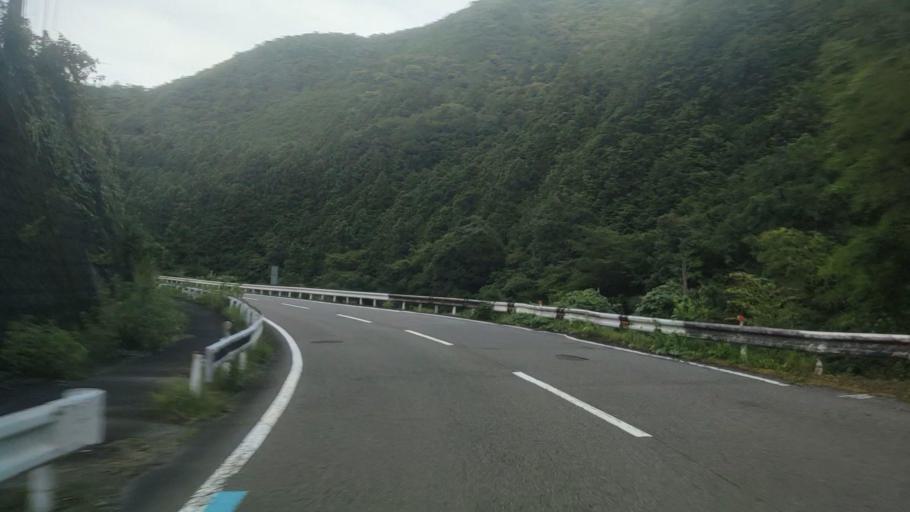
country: JP
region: Wakayama
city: Shingu
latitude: 33.8058
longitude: 135.7341
